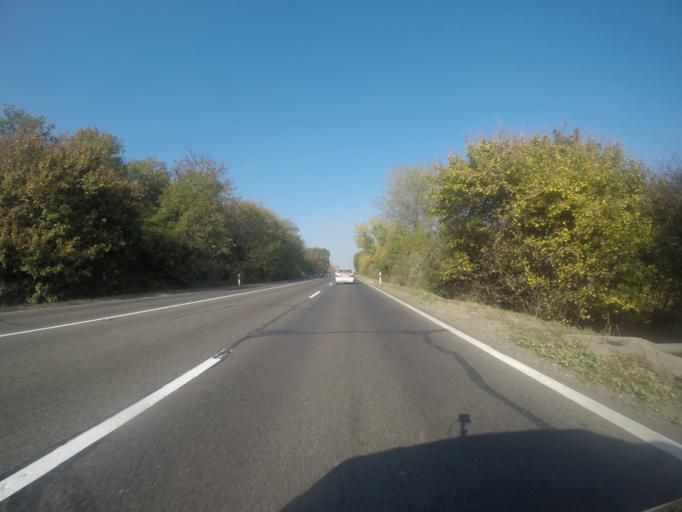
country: HU
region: Fejer
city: Baracs
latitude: 46.9200
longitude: 18.9294
